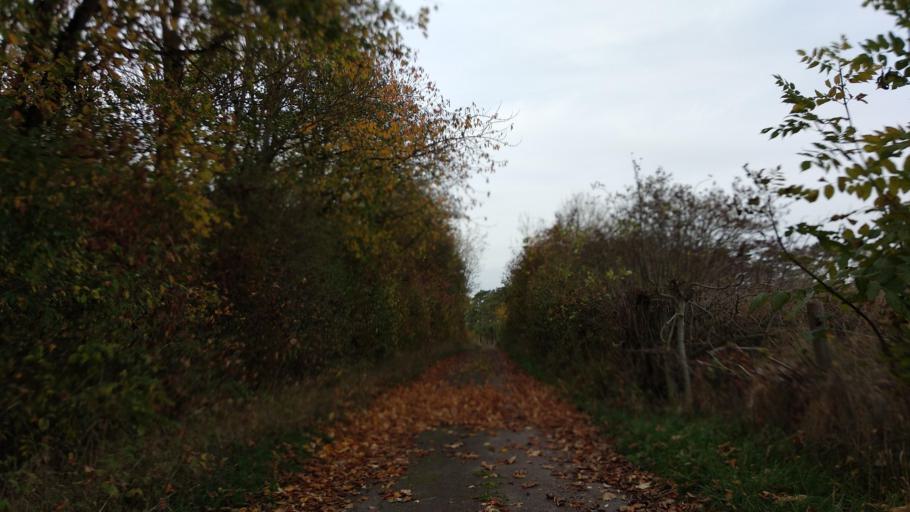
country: DE
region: North Rhine-Westphalia
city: Beverungen
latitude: 51.6876
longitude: 9.3349
